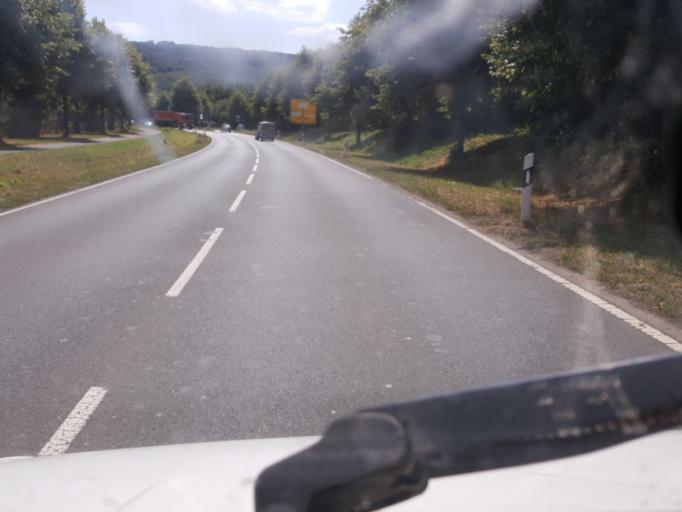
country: DE
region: North Rhine-Westphalia
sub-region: Regierungsbezirk Detmold
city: Minden
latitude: 52.2619
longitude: 8.8947
